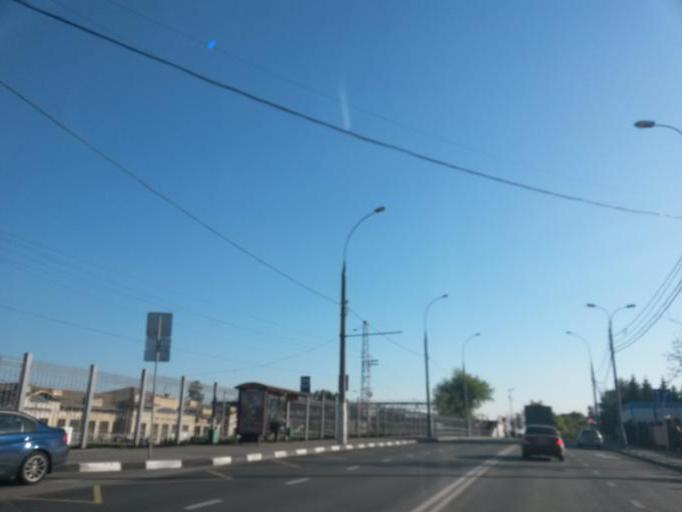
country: RU
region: Moscow
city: Orekhovo-Borisovo Severnoye
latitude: 55.6190
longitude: 37.6681
